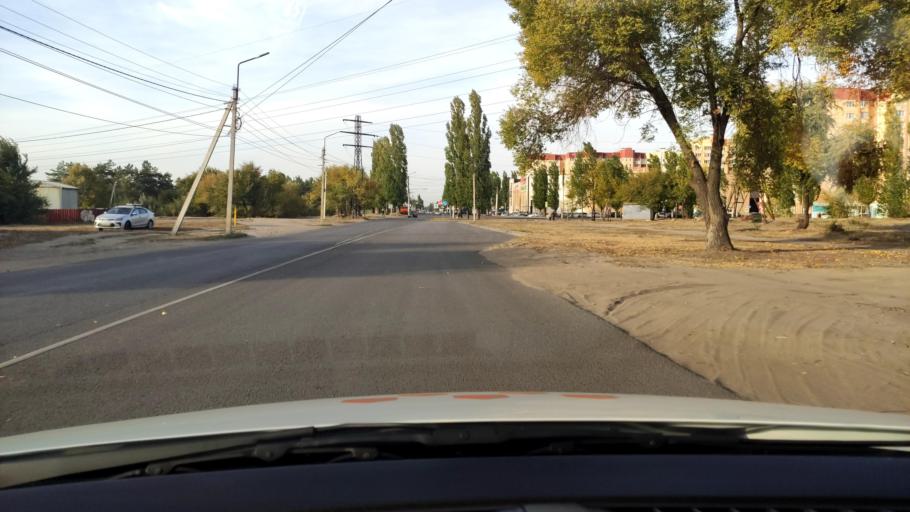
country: RU
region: Voronezj
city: Maslovka
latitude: 51.6005
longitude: 39.2369
